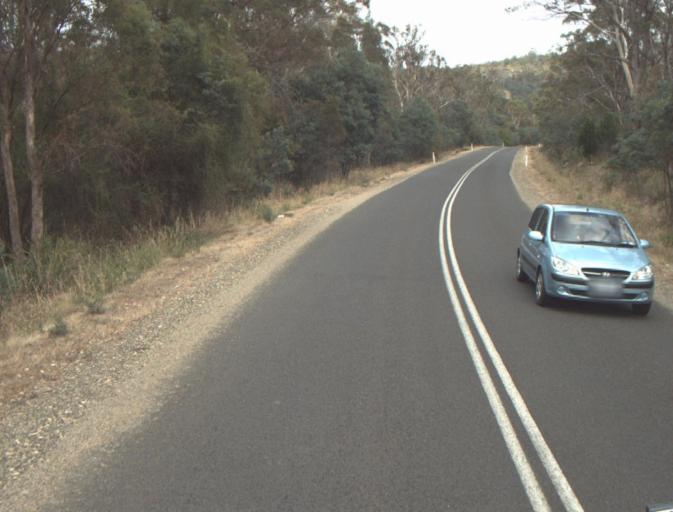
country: AU
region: Tasmania
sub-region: Northern Midlands
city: Evandale
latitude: -41.5091
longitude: 147.3500
